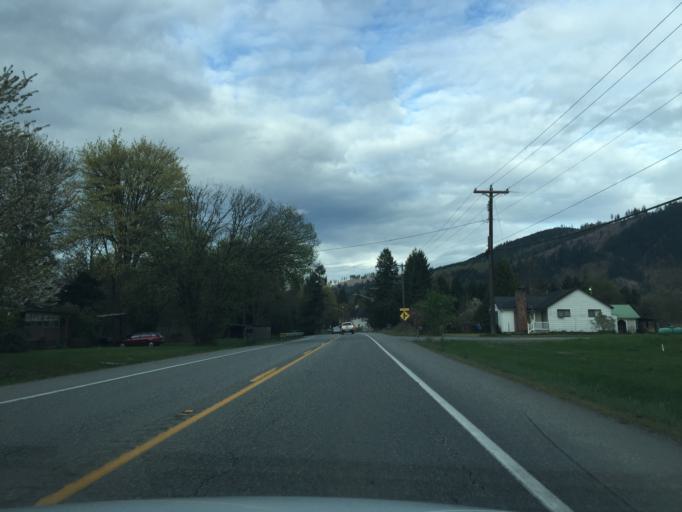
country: US
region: Washington
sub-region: Snohomish County
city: Arlington Heights
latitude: 48.2355
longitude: -122.0640
